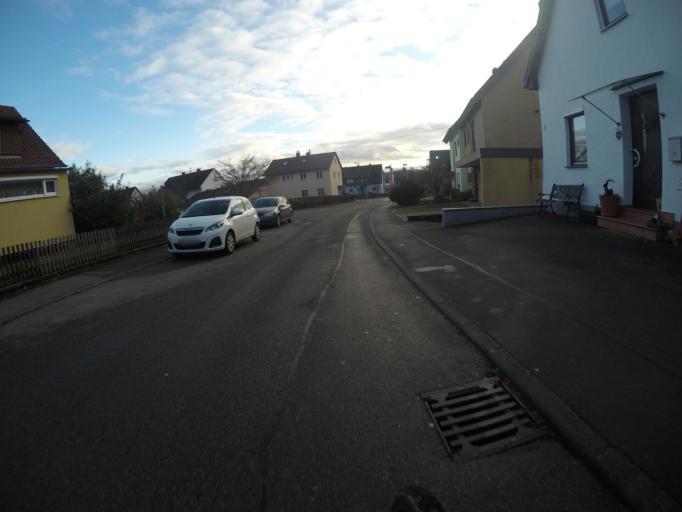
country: DE
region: Baden-Wuerttemberg
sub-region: Tuebingen Region
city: Tuebingen
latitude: 48.5022
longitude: 9.0000
